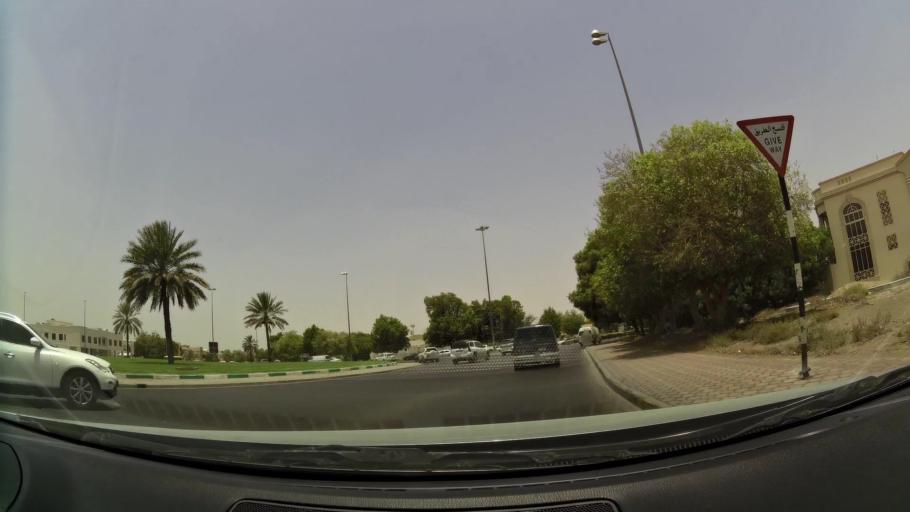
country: AE
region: Abu Dhabi
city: Al Ain
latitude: 24.2051
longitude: 55.7475
